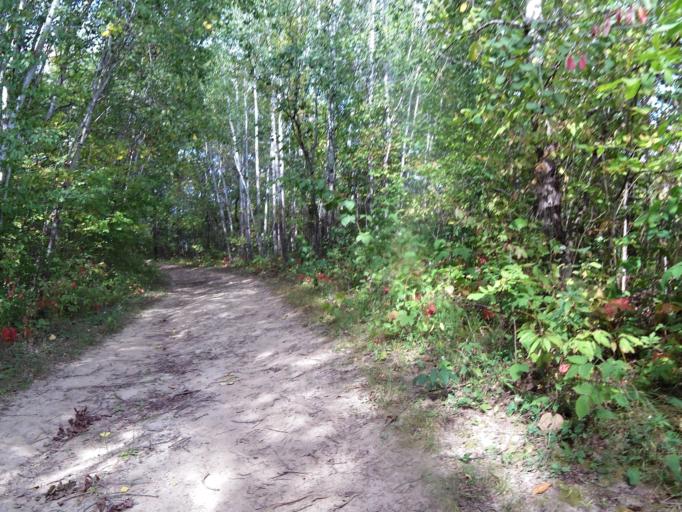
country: US
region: Minnesota
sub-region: Washington County
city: Afton
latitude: 44.8685
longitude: -92.7955
